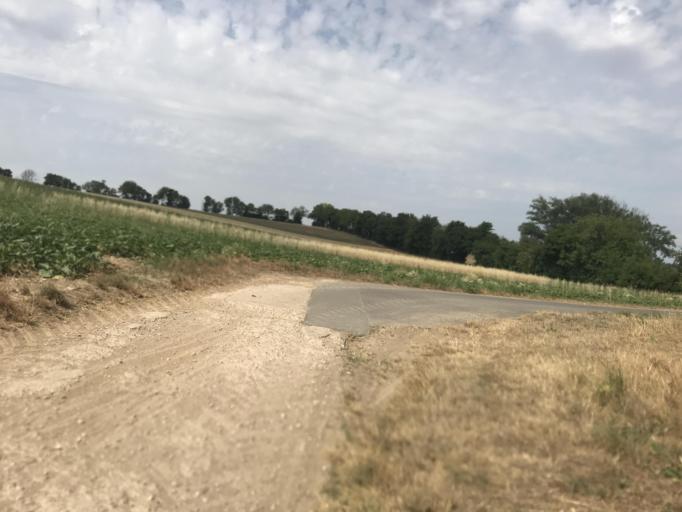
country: DE
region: Rheinland-Pfalz
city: Sorgenloch
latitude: 49.8626
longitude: 8.2078
